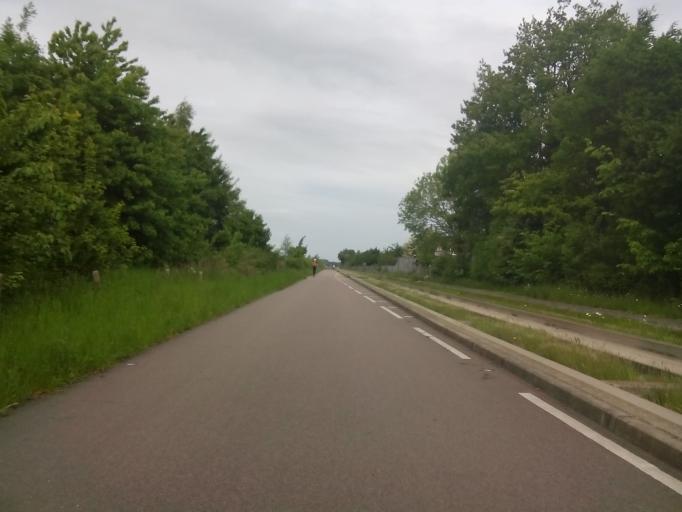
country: GB
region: England
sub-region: Cambridgeshire
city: Histon
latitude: 52.2507
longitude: 0.0967
